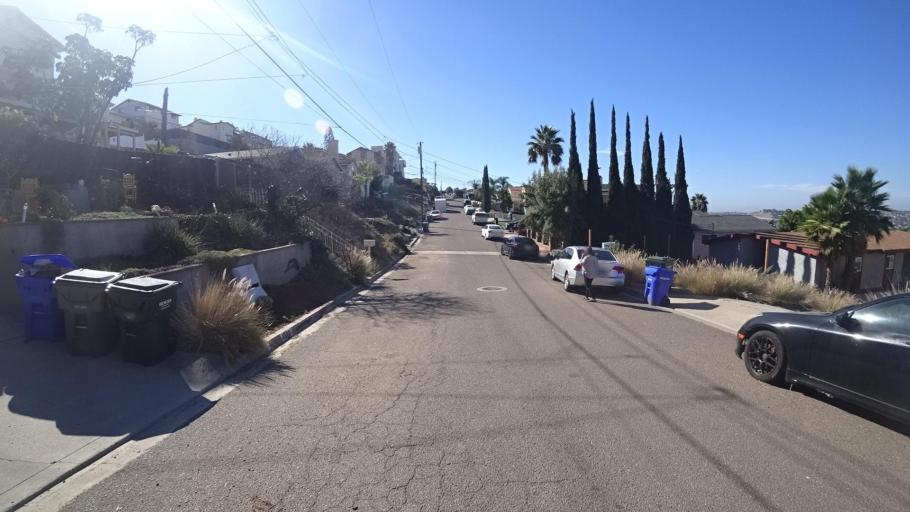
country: US
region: California
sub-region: San Diego County
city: La Presa
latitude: 32.7181
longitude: -116.9873
